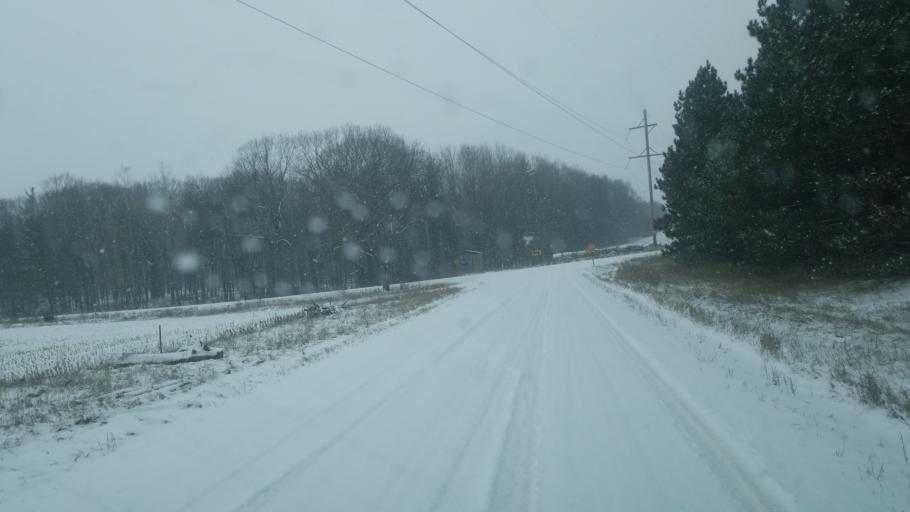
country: US
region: Michigan
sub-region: Osceola County
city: Reed City
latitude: 43.8427
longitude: -85.4141
